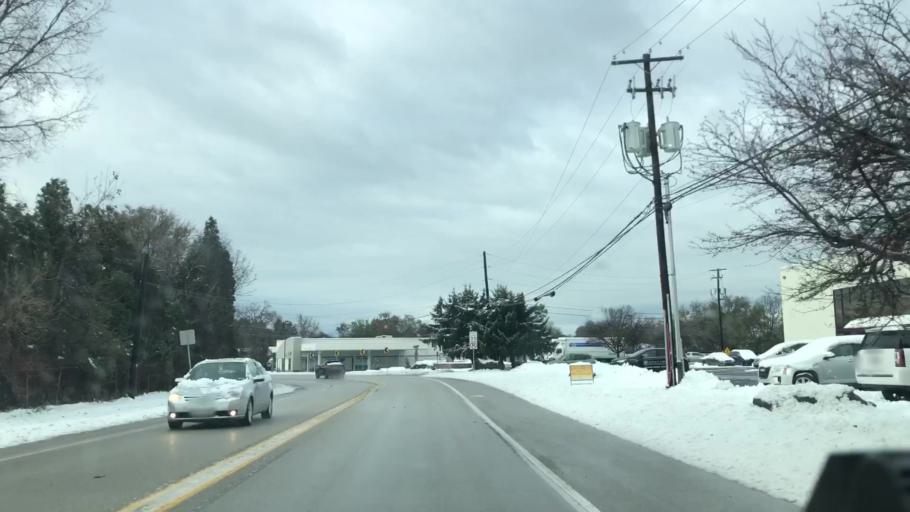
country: US
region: Pennsylvania
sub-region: Cumberland County
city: Shiremanstown
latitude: 40.2147
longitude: -76.9427
